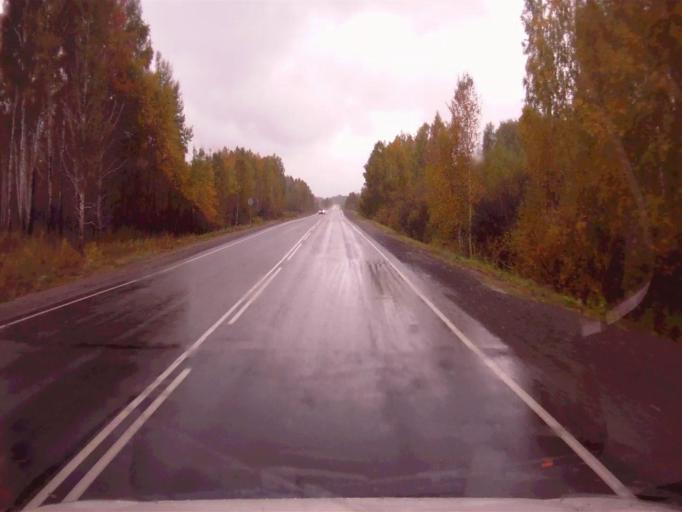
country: RU
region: Chelyabinsk
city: Argayash
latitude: 55.4797
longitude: 60.7580
